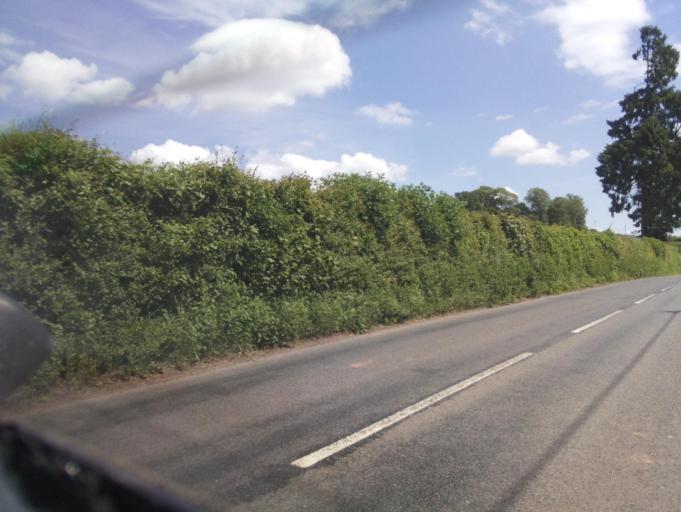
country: GB
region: Wales
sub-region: Monmouthshire
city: Monmouth
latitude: 51.8263
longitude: -2.7485
